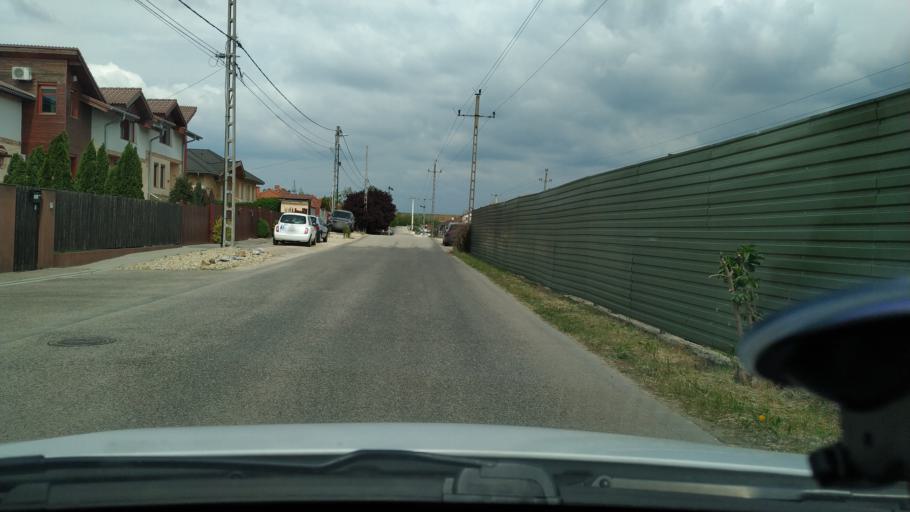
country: HU
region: Pest
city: Dunaharaszti
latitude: 47.3647
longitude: 19.1014
